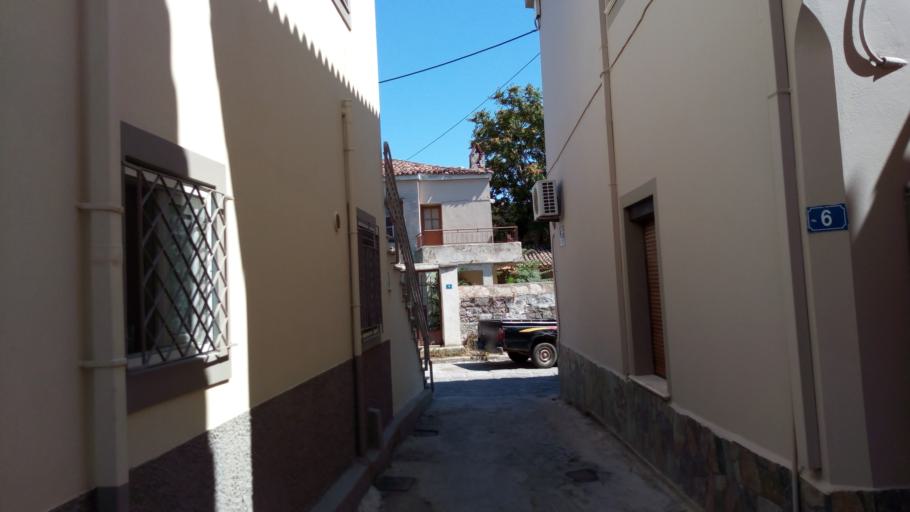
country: GR
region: North Aegean
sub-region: Nomos Lesvou
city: Myrina
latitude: 39.8751
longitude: 25.0604
